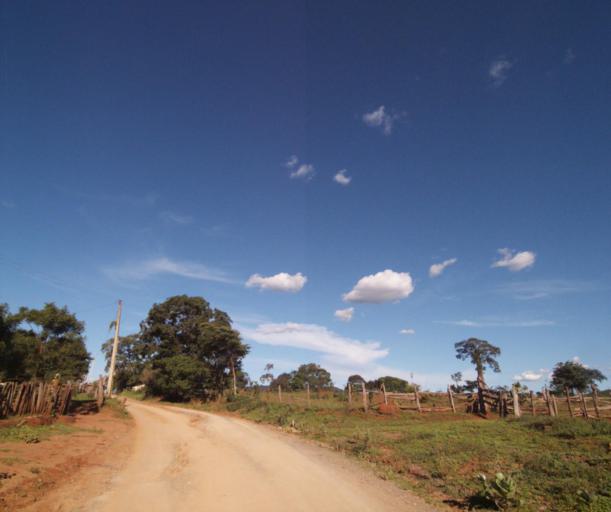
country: BR
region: Bahia
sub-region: Carinhanha
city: Carinhanha
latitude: -14.2854
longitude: -44.4841
